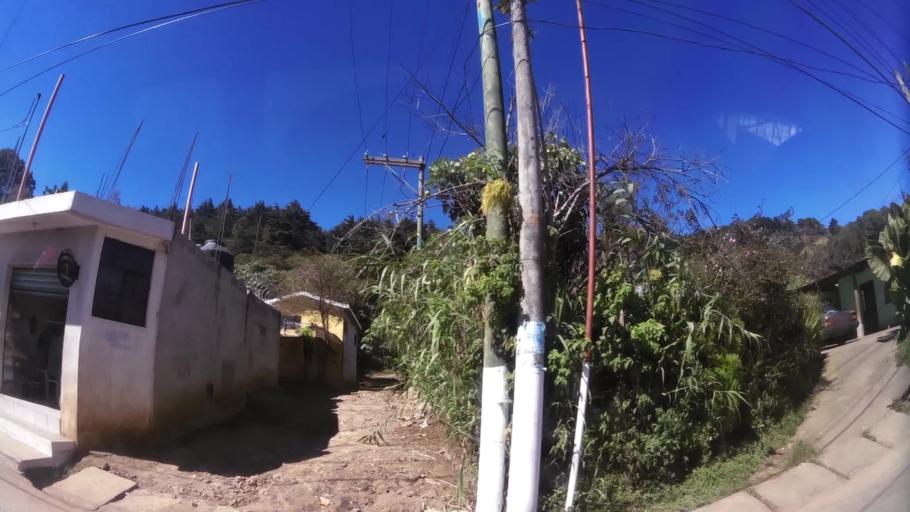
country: GT
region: Guatemala
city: San Jose Pinula
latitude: 14.5199
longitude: -90.4231
